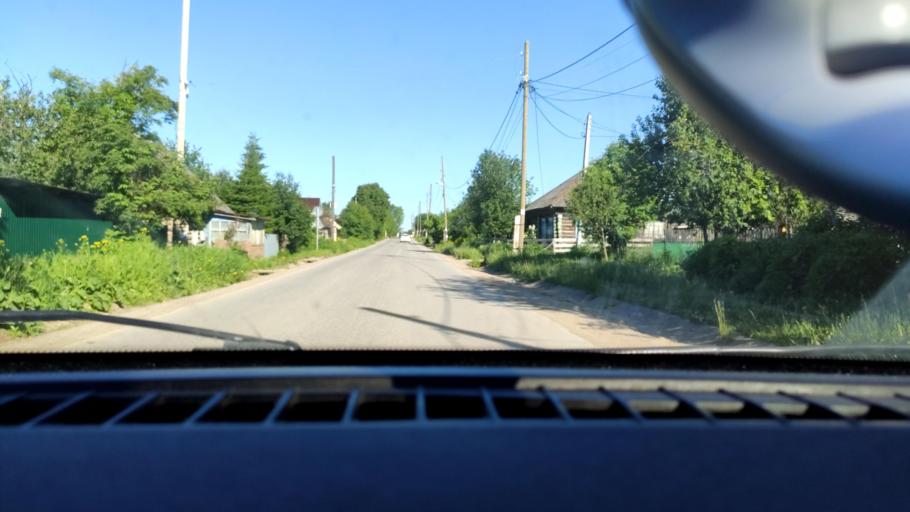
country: RU
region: Perm
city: Novyye Lyady
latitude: 58.1846
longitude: 56.5449
